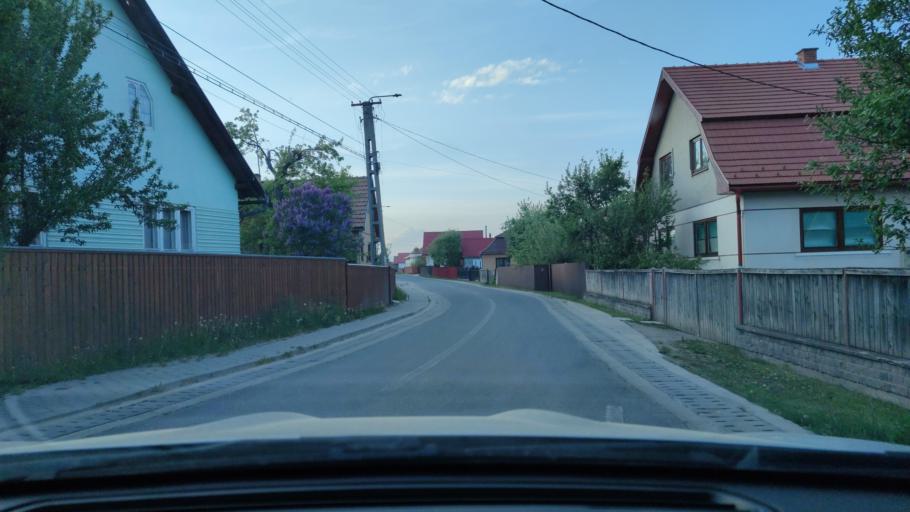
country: RO
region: Harghita
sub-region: Comuna Remetea
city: Remetea
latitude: 46.8016
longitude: 25.4506
